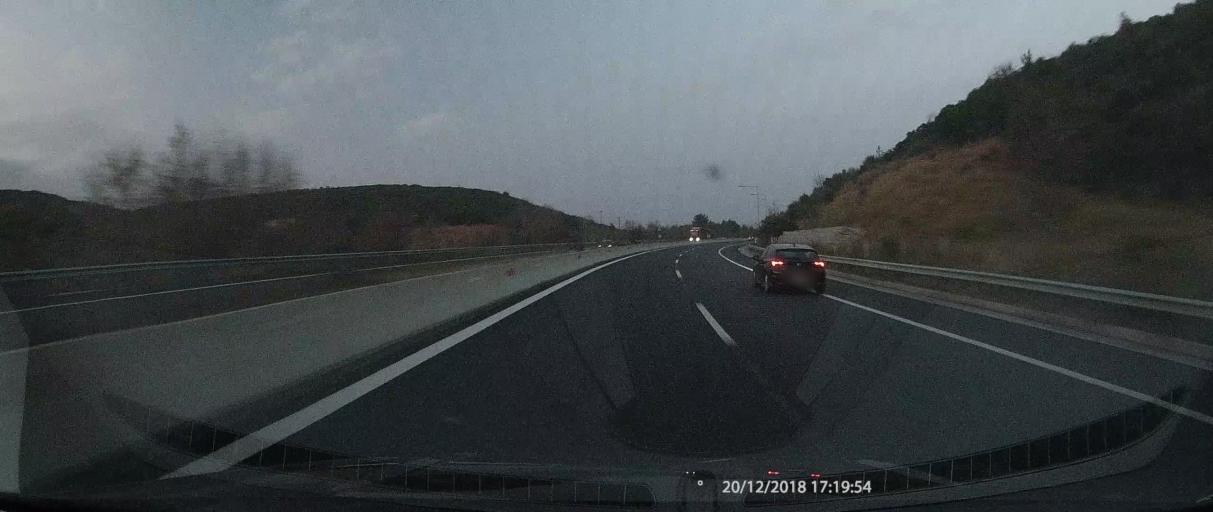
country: GR
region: Thessaly
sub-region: Nomos Larisis
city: Pyrgetos
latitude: 39.9546
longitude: 22.6456
